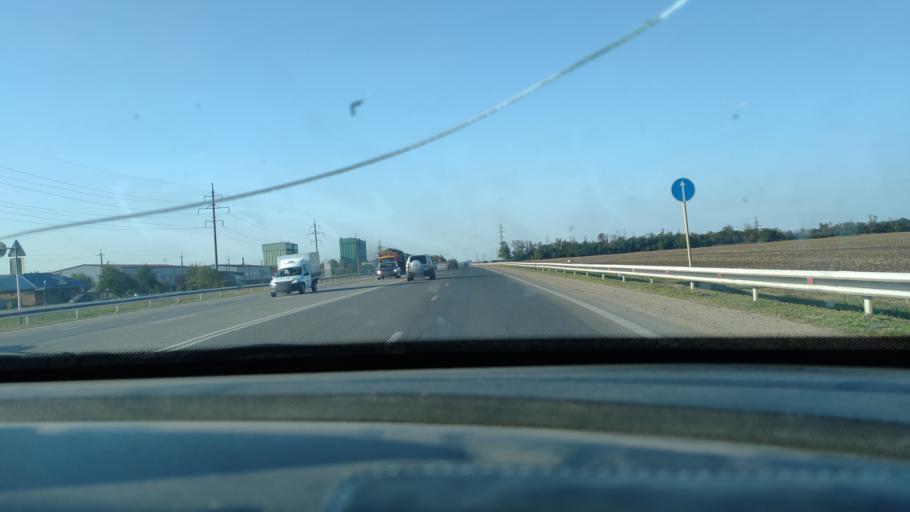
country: RU
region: Krasnodarskiy
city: Timashevsk
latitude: 45.6117
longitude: 38.9875
